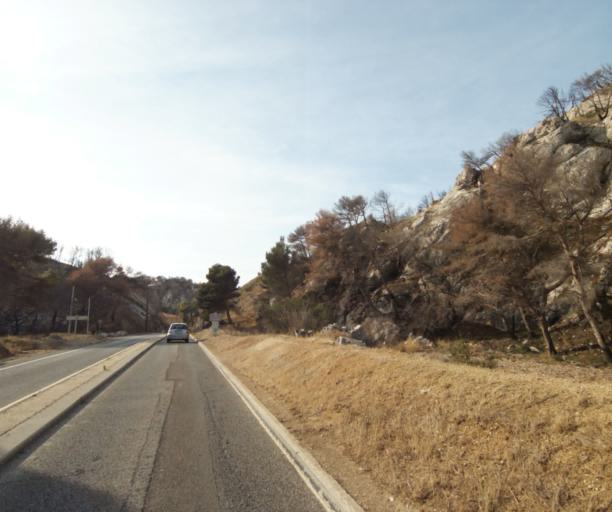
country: FR
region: Provence-Alpes-Cote d'Azur
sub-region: Departement des Bouches-du-Rhone
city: Carry-le-Rouet
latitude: 43.3384
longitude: 5.1785
